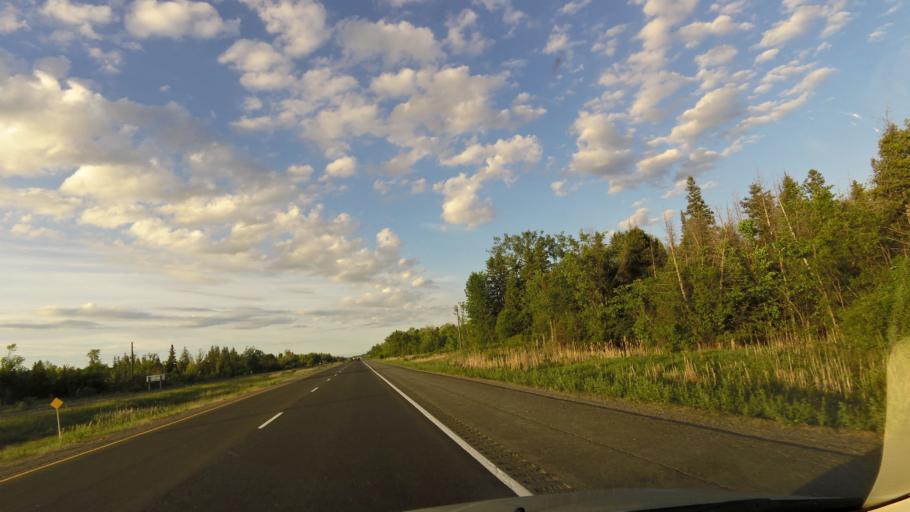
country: CA
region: Ontario
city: Peterborough
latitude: 44.2333
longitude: -78.3795
